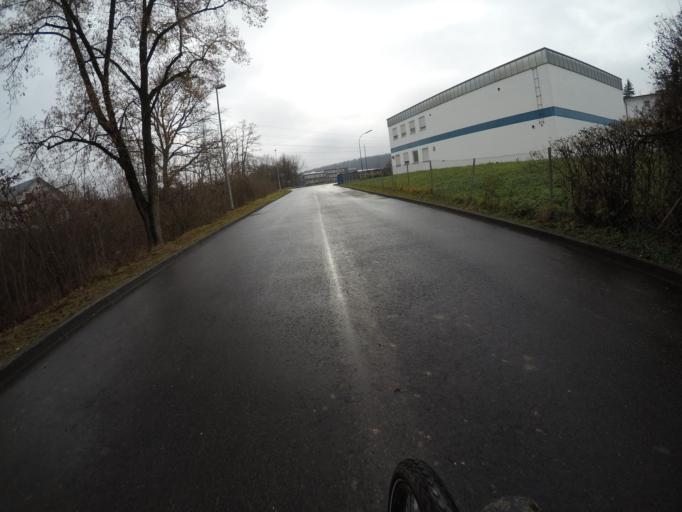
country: DE
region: Baden-Wuerttemberg
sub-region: Regierungsbezirk Stuttgart
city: Nurtingen
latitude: 48.6098
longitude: 9.3476
